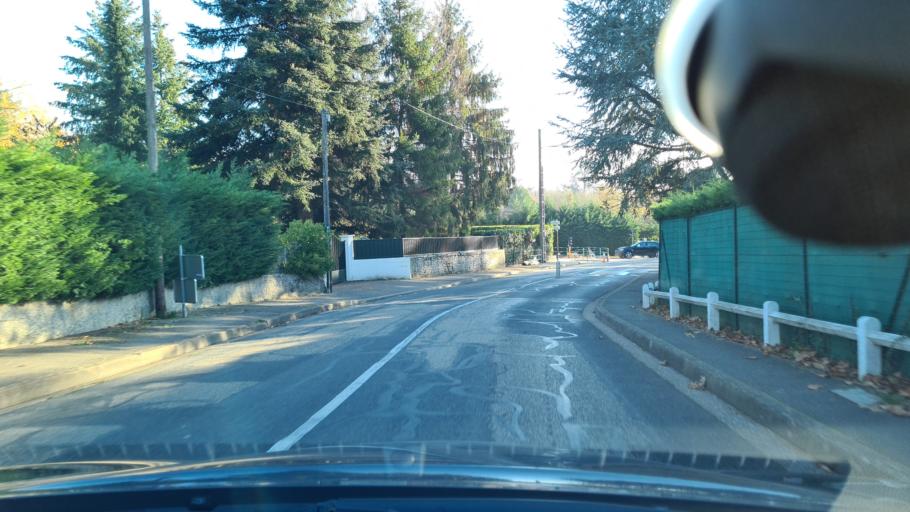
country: FR
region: Rhone-Alpes
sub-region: Departement du Rhone
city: Fontaines-sur-Saone
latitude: 45.8207
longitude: 4.8110
